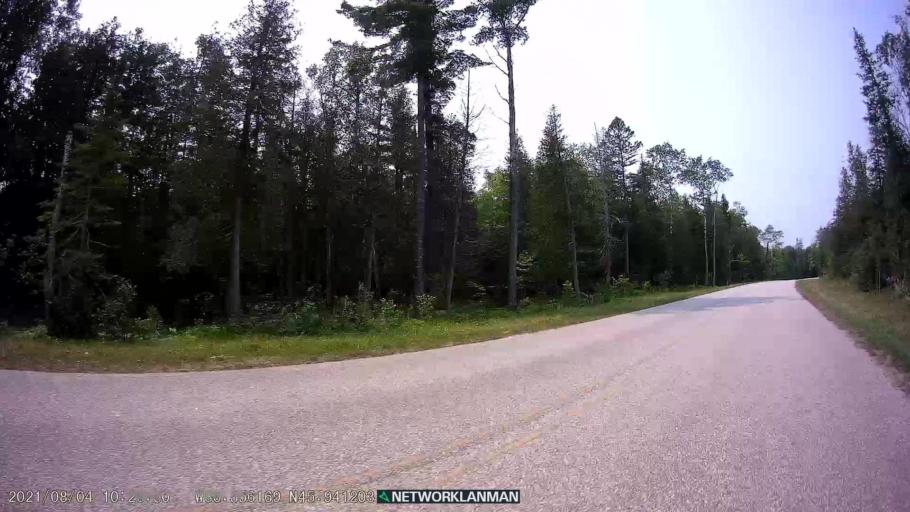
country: CA
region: Ontario
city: Thessalon
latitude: 45.9414
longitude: -83.5567
